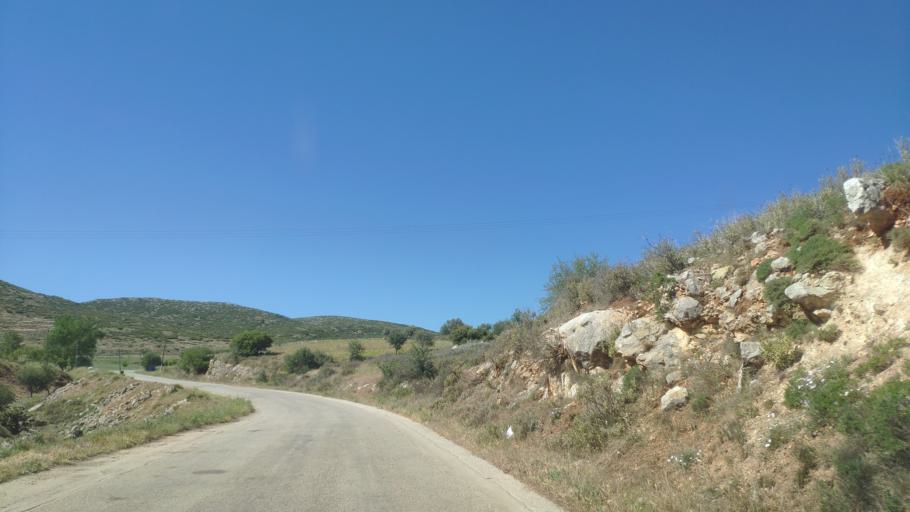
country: GR
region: Peloponnese
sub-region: Nomos Korinthias
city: Khiliomodhi
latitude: 37.7552
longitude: 22.8739
